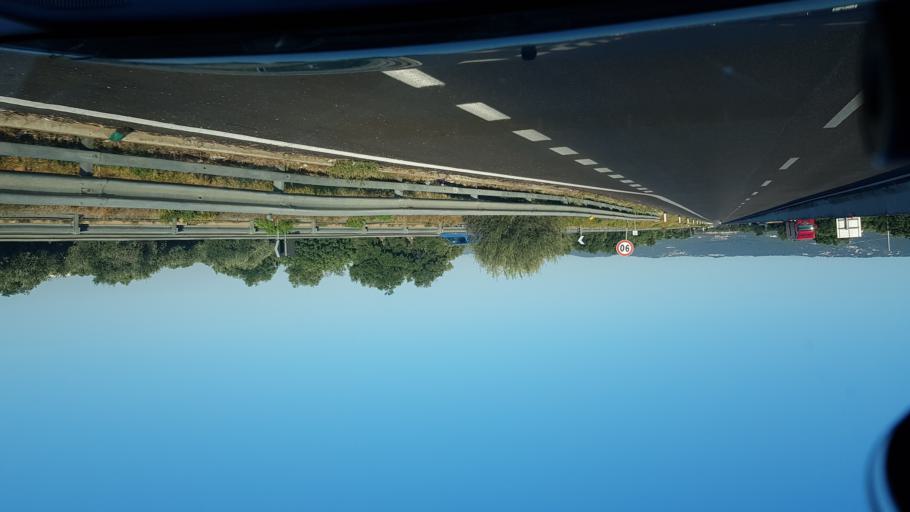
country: IT
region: Apulia
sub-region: Provincia di Brindisi
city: Pezze di Greco
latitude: 40.8340
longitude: 17.4031
